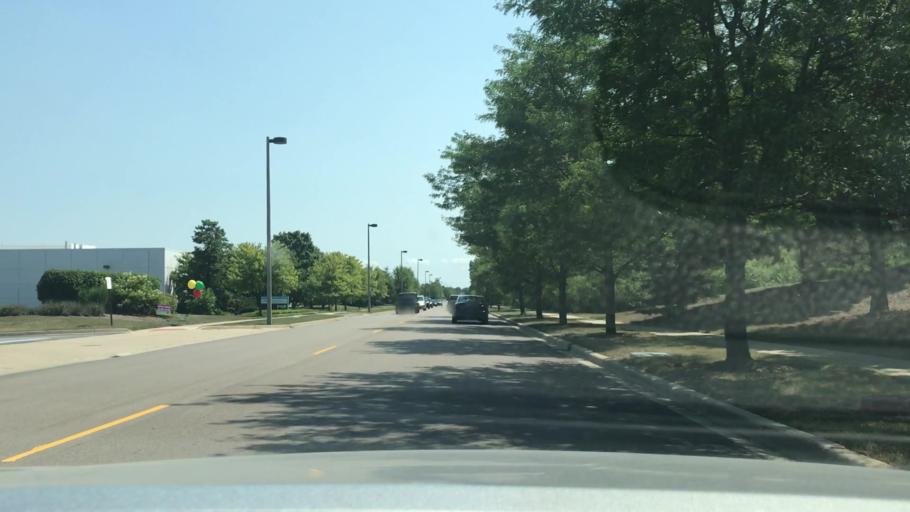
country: US
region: Illinois
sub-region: Kane County
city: Aurora
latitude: 41.7434
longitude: -88.2303
